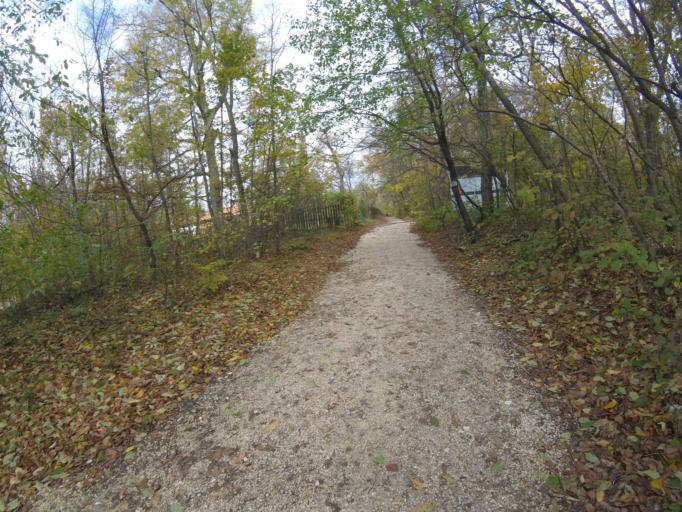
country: HU
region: Pest
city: Budakeszi
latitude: 47.5118
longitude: 18.9570
